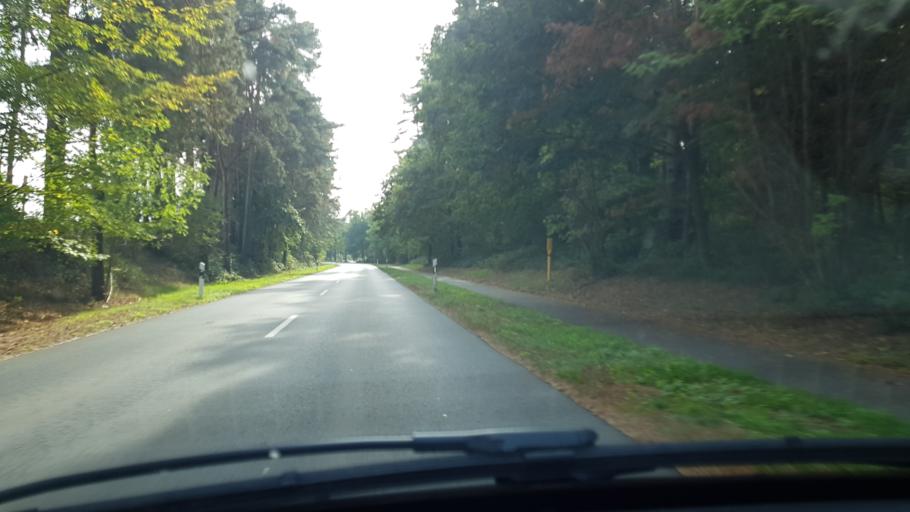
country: DE
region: Lower Saxony
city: Lehre
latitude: 52.3127
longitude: 10.6584
